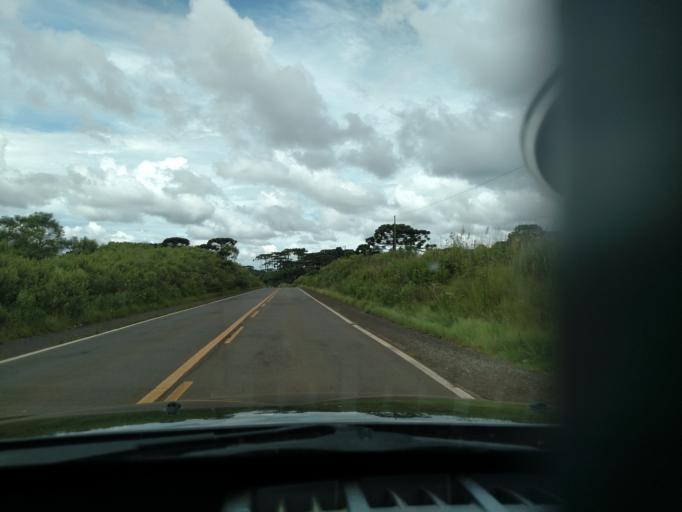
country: BR
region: Santa Catarina
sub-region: Lages
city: Lages
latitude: -27.9141
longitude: -50.5863
